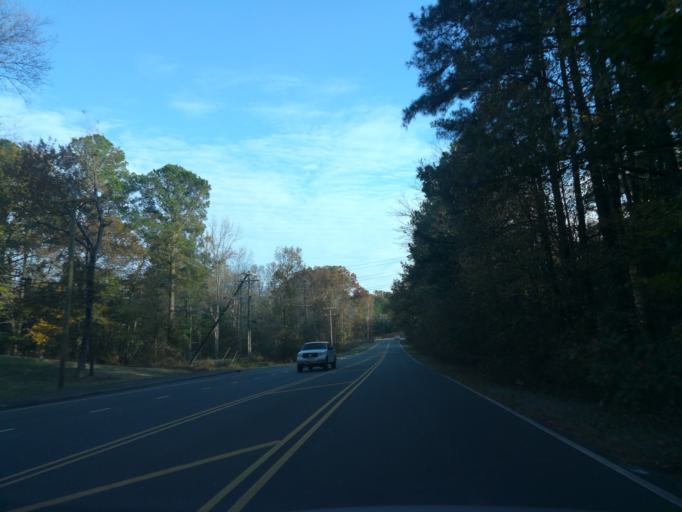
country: US
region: North Carolina
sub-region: Orange County
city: Chapel Hill
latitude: 35.9593
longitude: -78.9972
